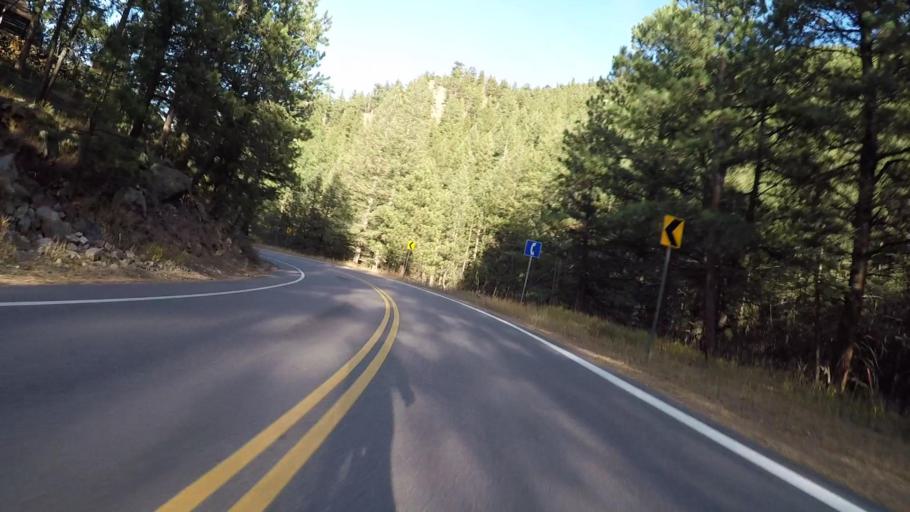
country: US
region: Colorado
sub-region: Boulder County
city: Boulder
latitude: 40.0986
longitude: -105.3442
